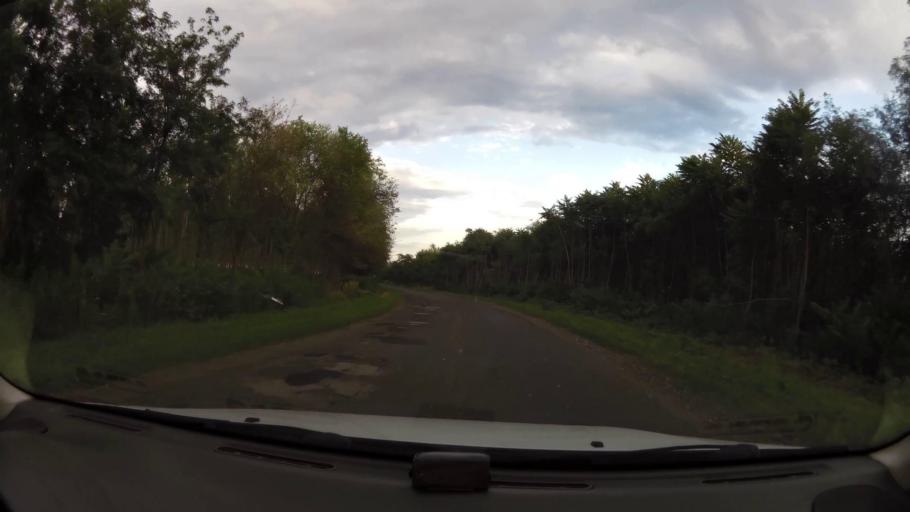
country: HU
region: Pest
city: Tapioszolos
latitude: 47.3224
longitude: 19.8297
